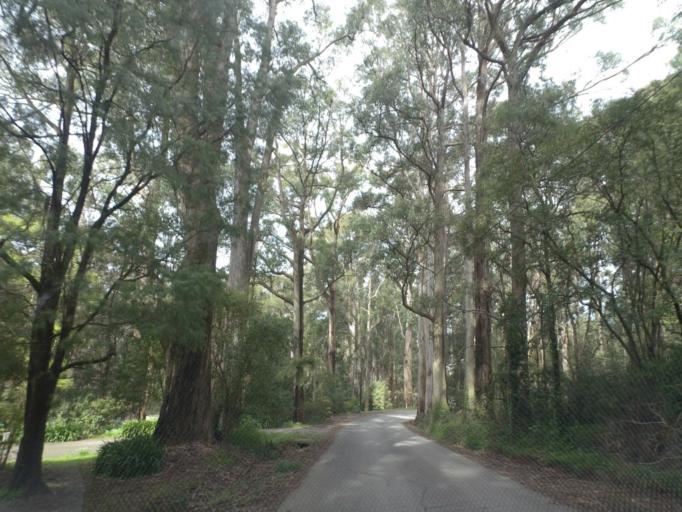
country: AU
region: Victoria
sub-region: Yarra Ranges
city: Mount Dandenong
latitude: -37.8334
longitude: 145.3692
